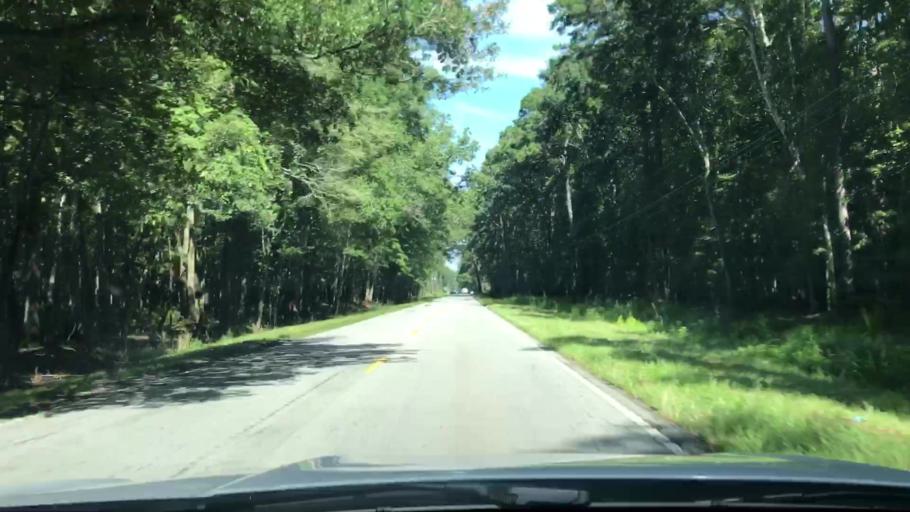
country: US
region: South Carolina
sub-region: Dorchester County
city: Centerville
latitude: 32.9320
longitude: -80.1741
